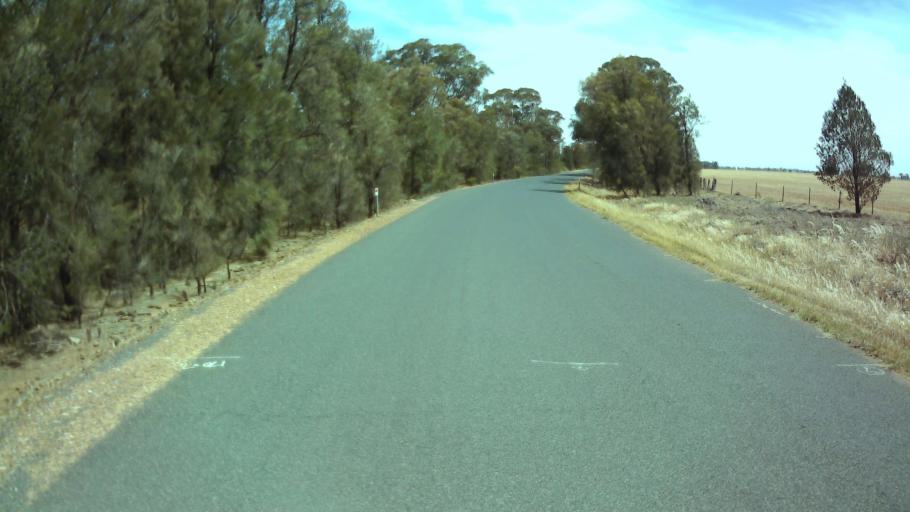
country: AU
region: New South Wales
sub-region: Weddin
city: Grenfell
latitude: -33.9458
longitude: 147.7788
